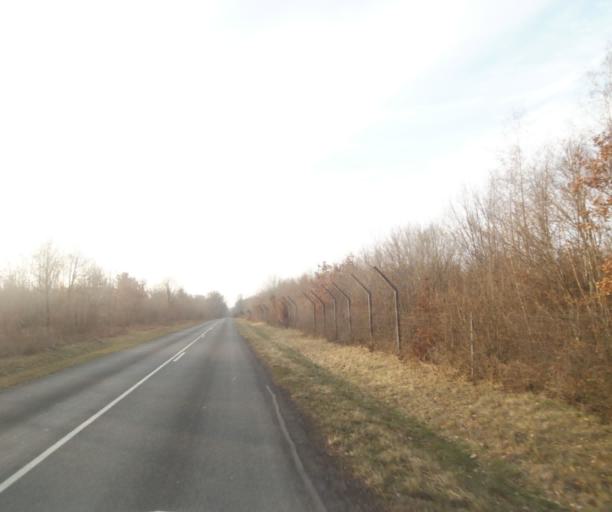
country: FR
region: Champagne-Ardenne
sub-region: Departement de la Haute-Marne
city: Bettancourt-la-Ferree
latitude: 48.6871
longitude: 4.9439
